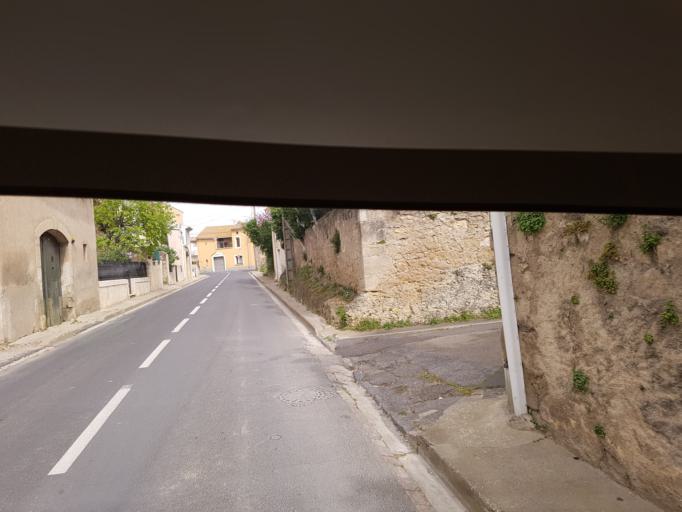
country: FR
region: Languedoc-Roussillon
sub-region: Departement de l'Herault
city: Lespignan
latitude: 43.2745
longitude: 3.1751
